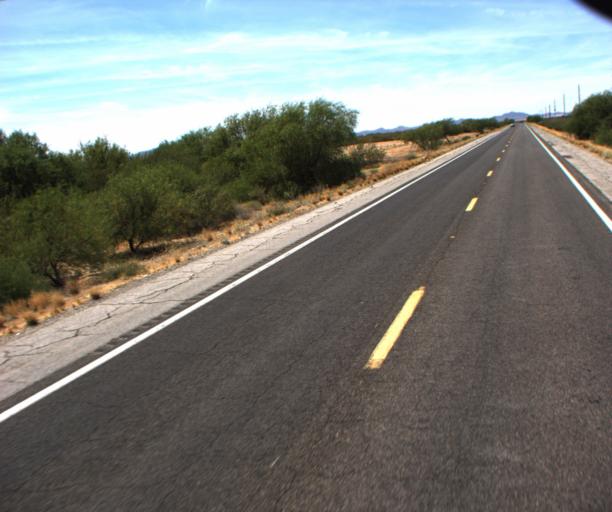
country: US
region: Arizona
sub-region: La Paz County
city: Salome
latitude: 33.8318
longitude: -113.5039
